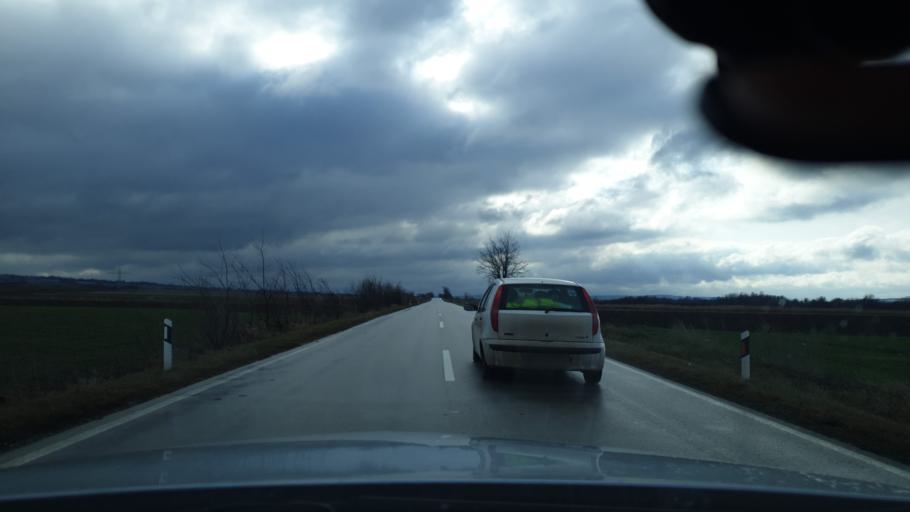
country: RS
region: Central Serbia
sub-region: Branicevski Okrug
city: Malo Crnice
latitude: 44.4908
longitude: 21.3284
